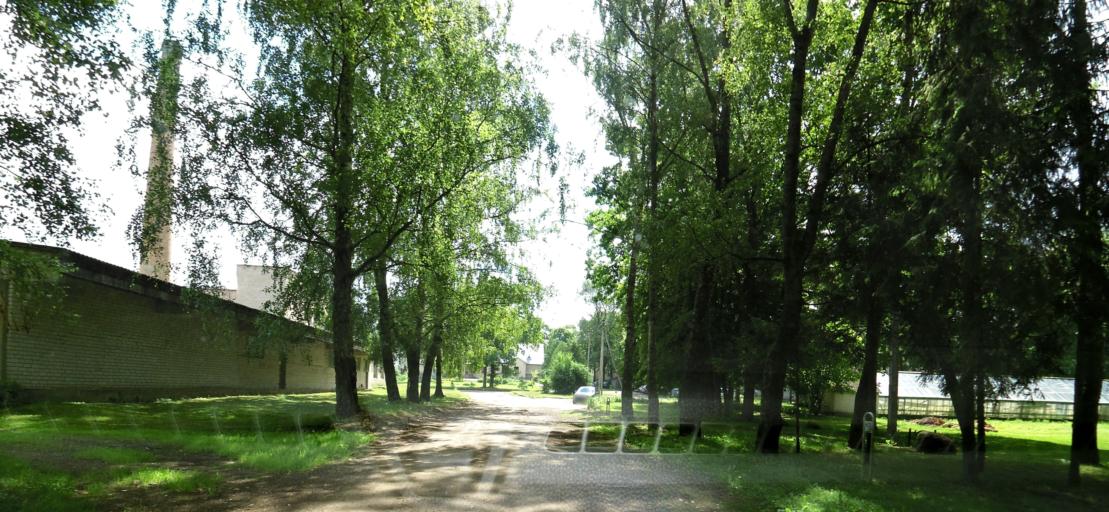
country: LT
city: Vabalninkas
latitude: 55.9797
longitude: 24.7429
